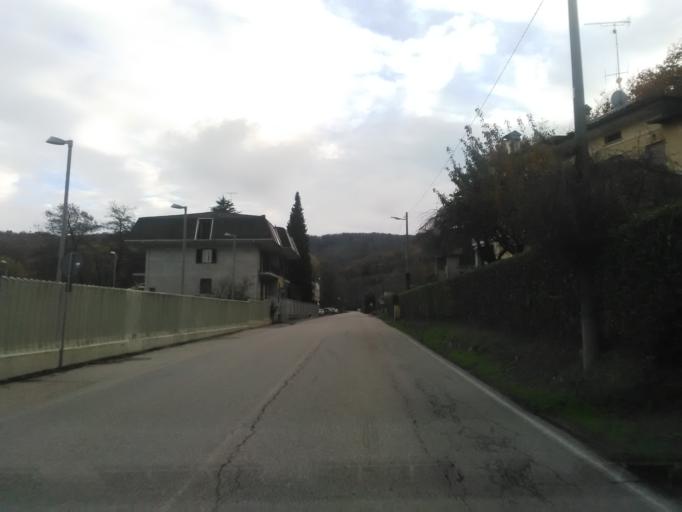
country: IT
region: Piedmont
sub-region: Provincia di Novara
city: Pogno
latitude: 45.7517
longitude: 8.3810
